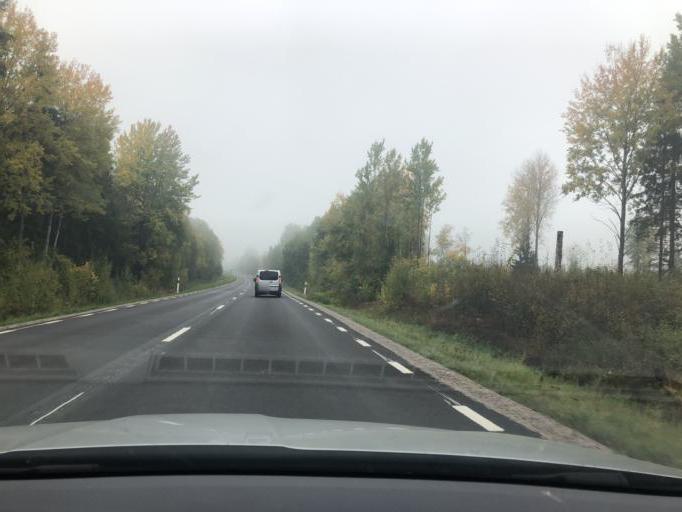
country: SE
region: Uppsala
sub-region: Tierps Kommun
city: Tierp
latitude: 60.2816
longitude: 17.5914
